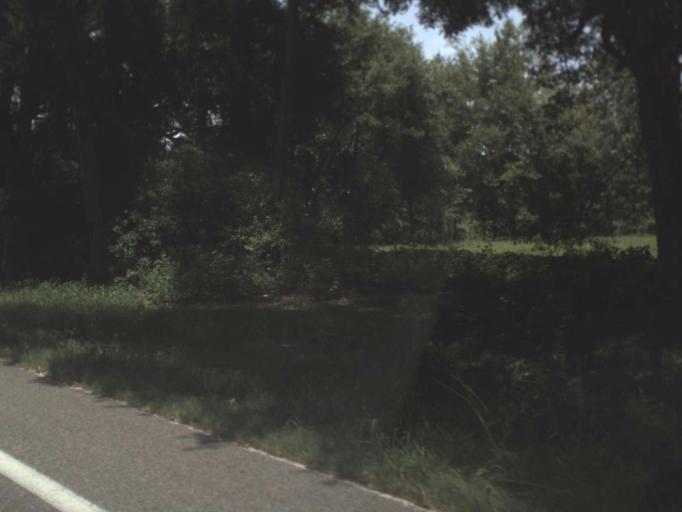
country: US
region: Florida
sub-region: Gilchrist County
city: Trenton
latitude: 29.6862
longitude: -82.8573
